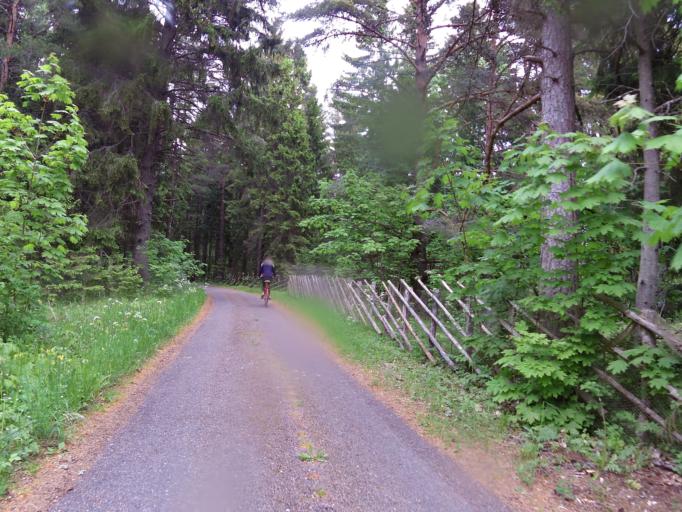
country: EE
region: Harju
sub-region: Paldiski linn
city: Paldiski
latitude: 59.2578
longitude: 23.7457
